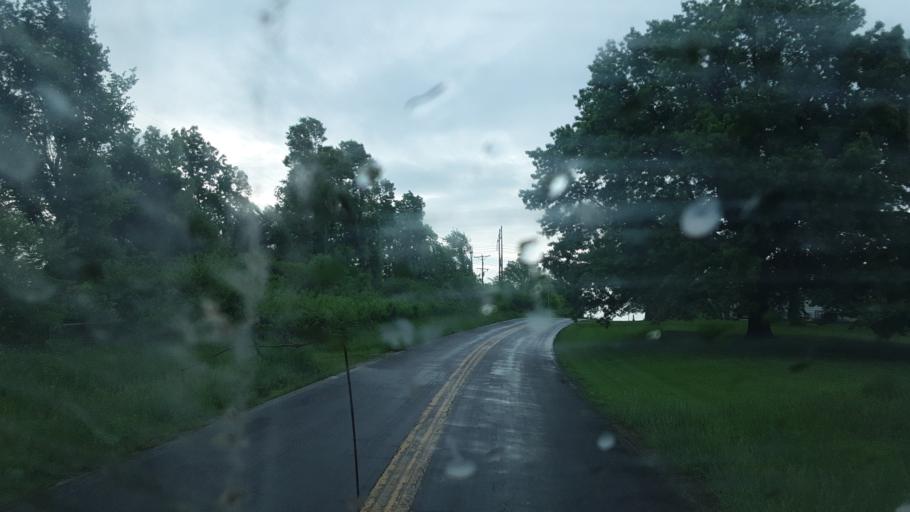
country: US
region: Missouri
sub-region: Clark County
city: Kahoka
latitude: 40.4343
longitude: -91.5870
